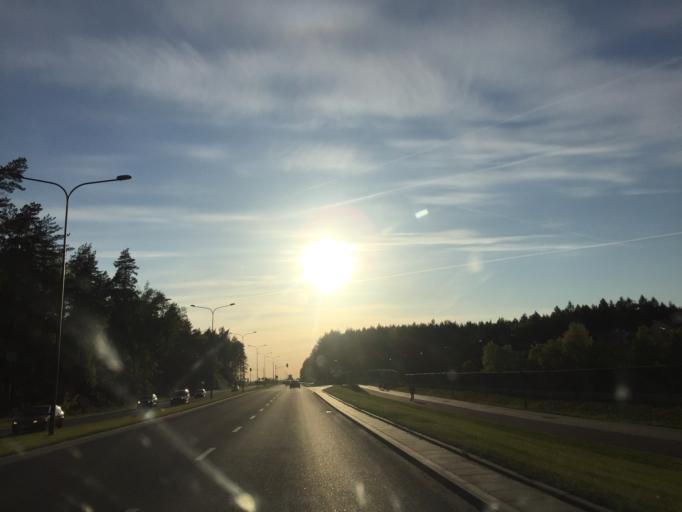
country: PL
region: Pomeranian Voivodeship
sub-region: Sopot
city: Sopot
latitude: 54.3770
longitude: 18.5058
